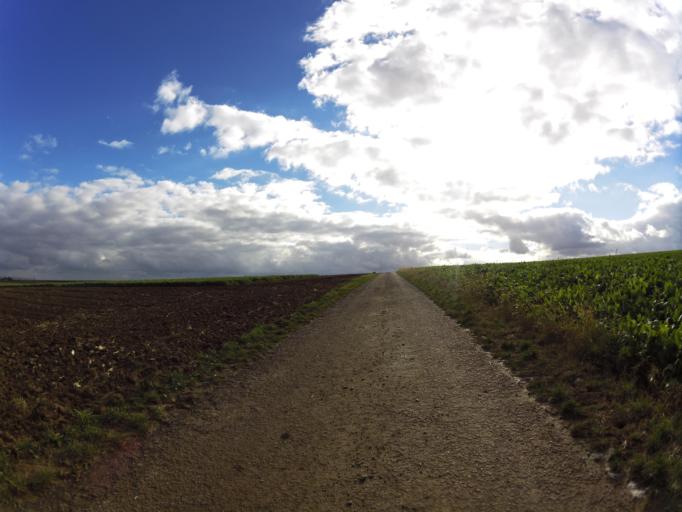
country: DE
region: Bavaria
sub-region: Regierungsbezirk Unterfranken
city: Unterpleichfeld
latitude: 49.8786
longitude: 10.0115
